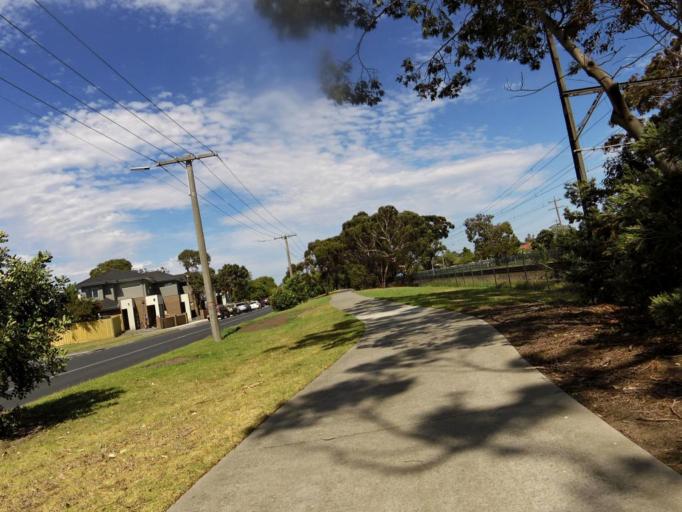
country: AU
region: Victoria
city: Clayton
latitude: -37.9187
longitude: 145.1129
